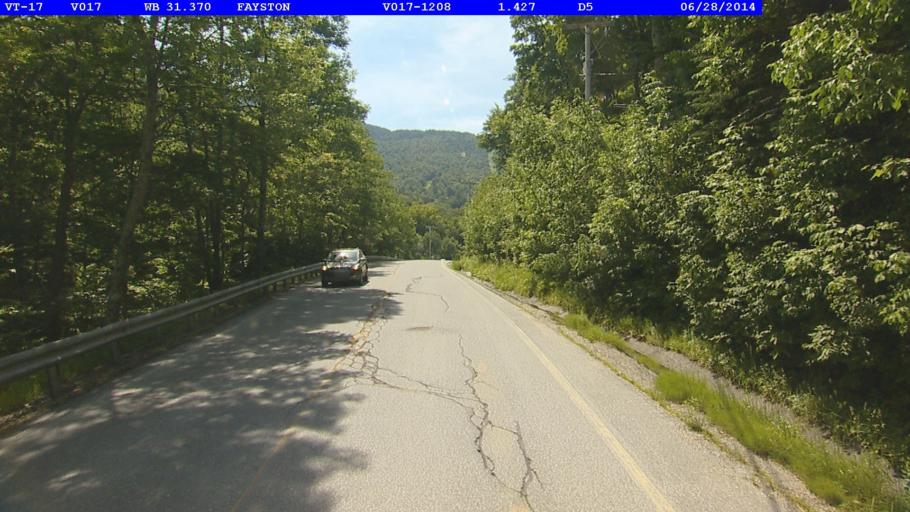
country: US
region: Vermont
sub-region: Addison County
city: Bristol
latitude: 44.2019
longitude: -72.9135
